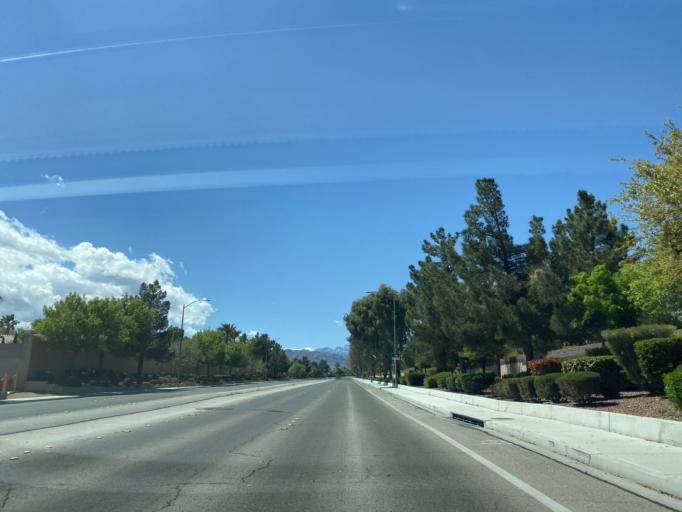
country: US
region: Nevada
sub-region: Clark County
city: North Las Vegas
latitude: 36.2979
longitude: -115.2552
